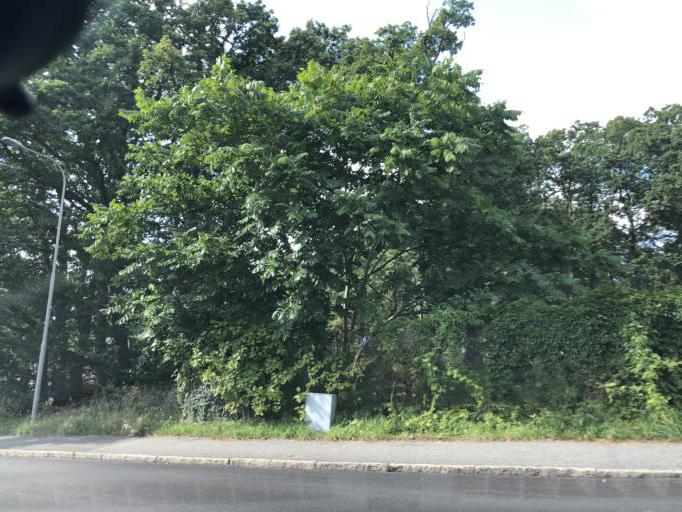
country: SE
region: Vaestra Goetaland
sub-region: Goteborg
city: Goeteborg
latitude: 57.7477
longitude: 11.9541
